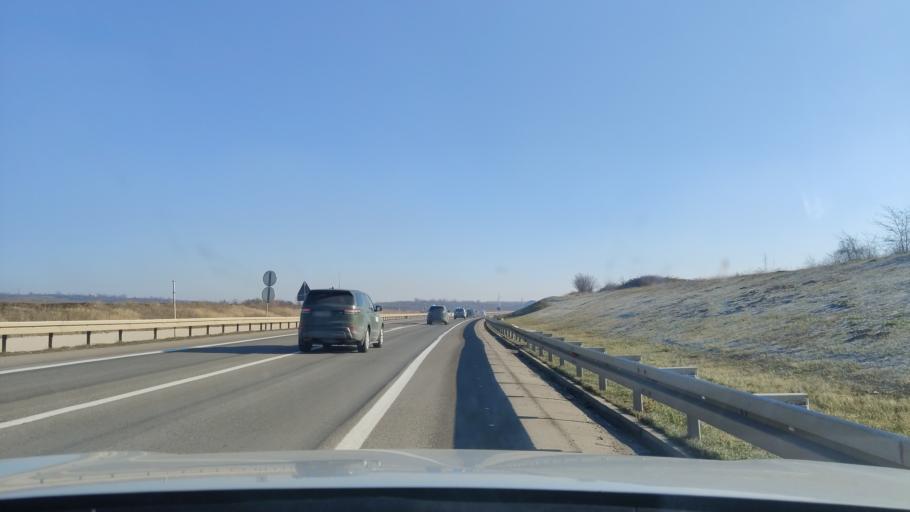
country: RS
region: Central Serbia
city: Sremcica
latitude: 44.7157
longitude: 20.3955
